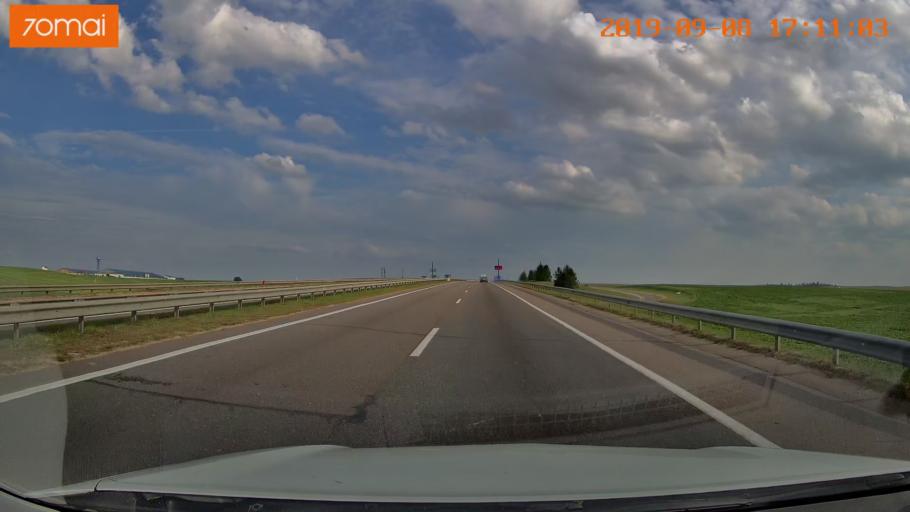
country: BY
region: Grodnenskaya
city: Hrodna
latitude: 53.6472
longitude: 23.9988
